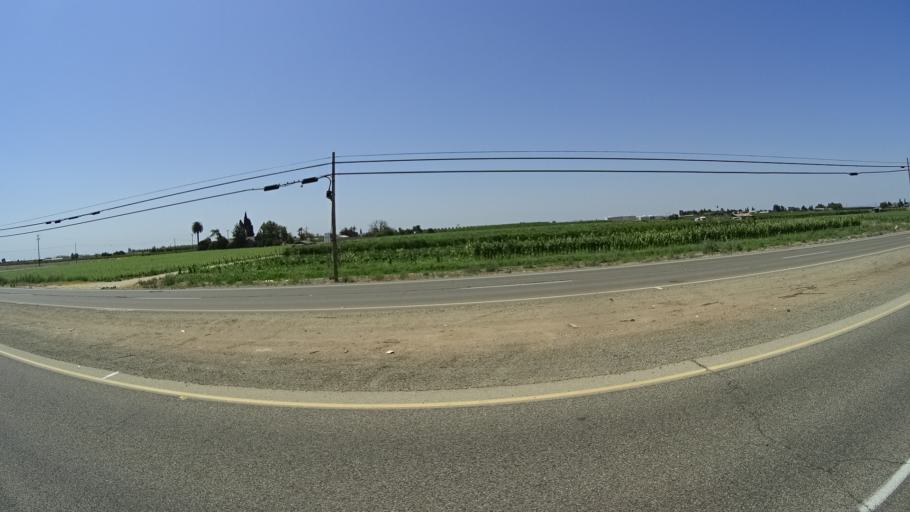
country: US
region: California
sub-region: Fresno County
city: Sunnyside
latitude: 36.7076
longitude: -119.6749
